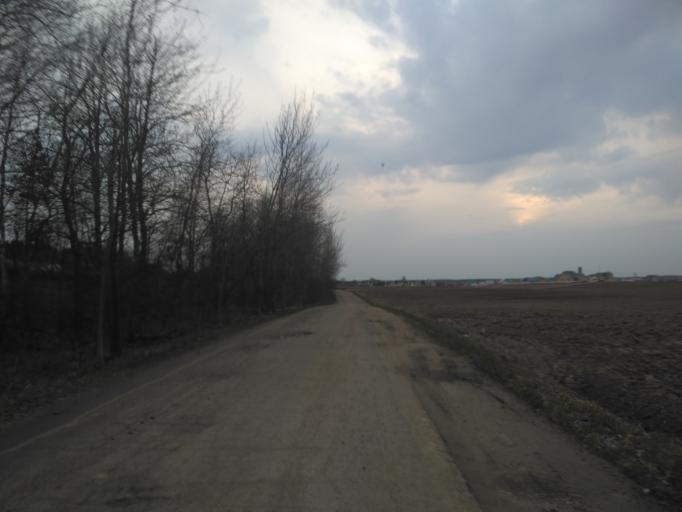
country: BY
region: Minsk
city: Slabada
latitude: 53.9952
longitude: 27.9044
